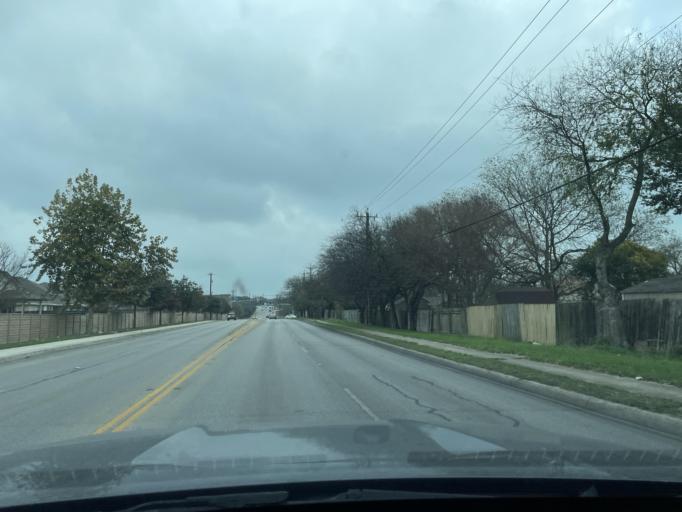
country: US
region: Texas
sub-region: Bexar County
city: Leon Valley
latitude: 29.5572
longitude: -98.6221
